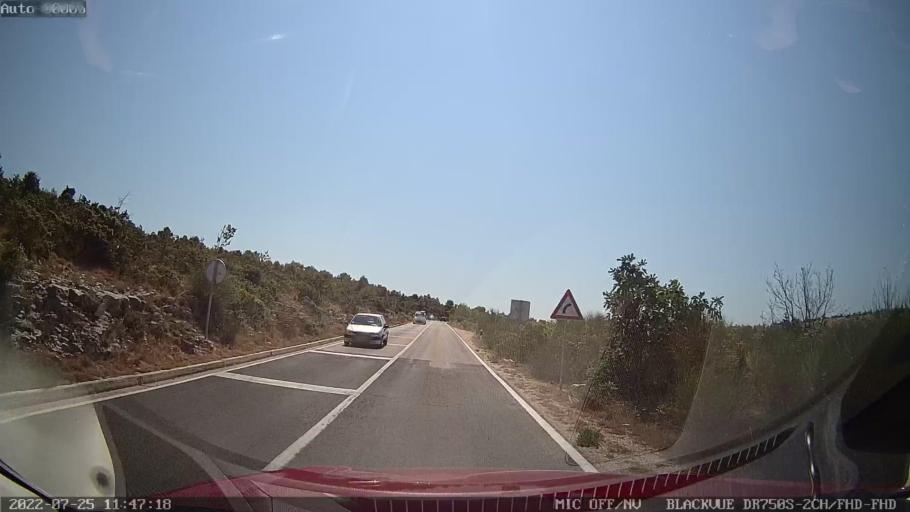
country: HR
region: Zadarska
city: Razanac
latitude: 44.2394
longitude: 15.3004
